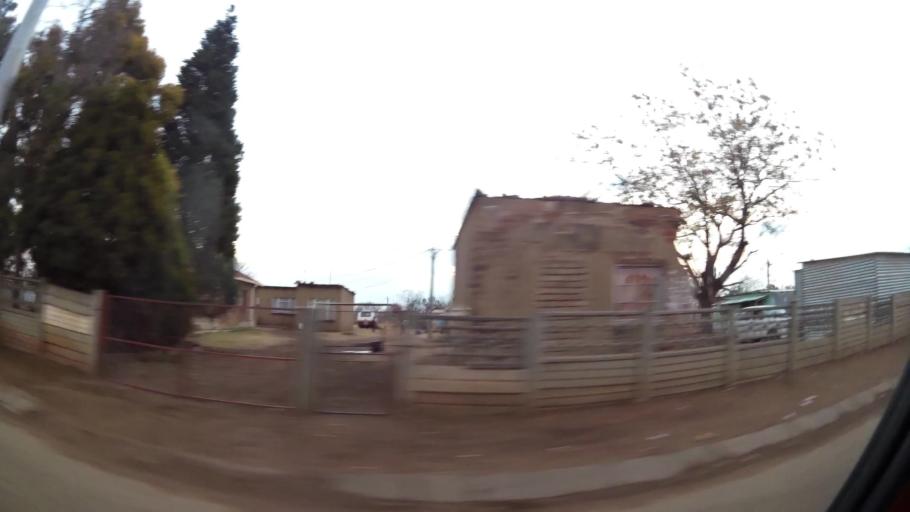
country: ZA
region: Gauteng
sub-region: City of Johannesburg Metropolitan Municipality
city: Orange Farm
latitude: -26.5509
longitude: 27.8487
